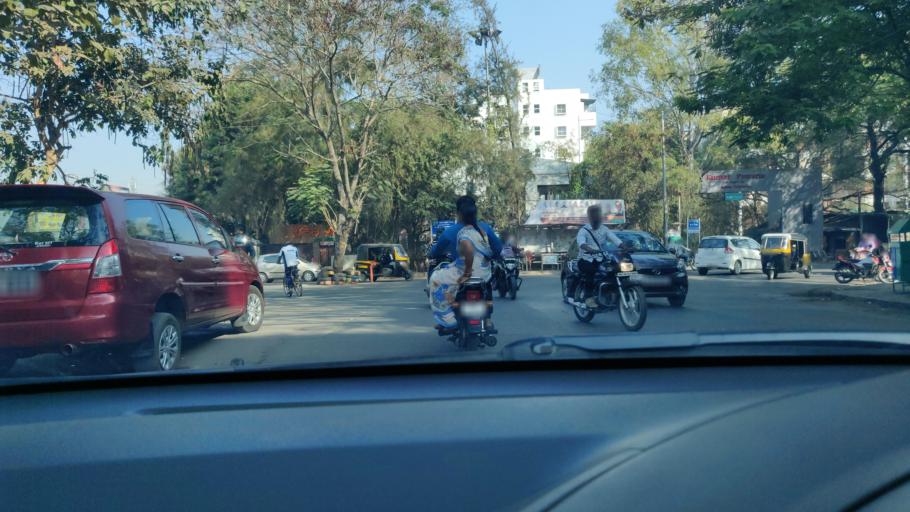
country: IN
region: Maharashtra
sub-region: Pune Division
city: Khadki
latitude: 18.5653
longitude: 73.8024
